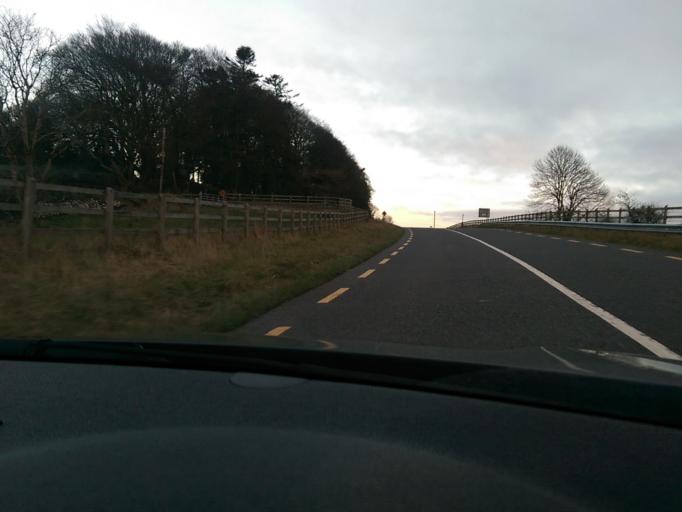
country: IE
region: Connaught
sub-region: Sligo
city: Ballymote
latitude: 53.9822
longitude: -8.4673
